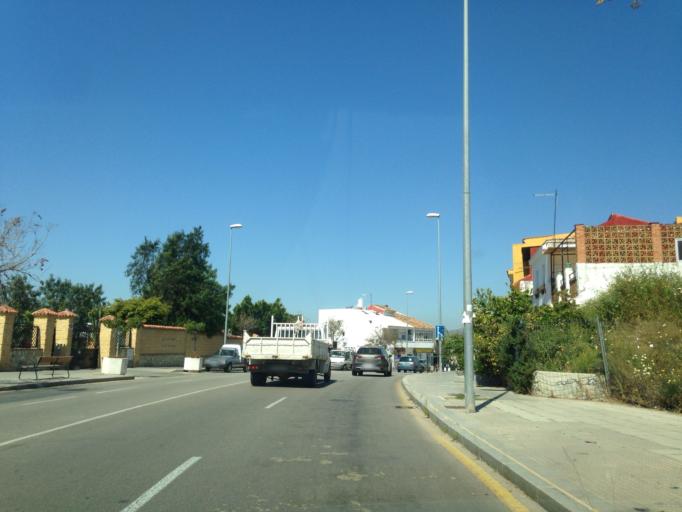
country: ES
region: Andalusia
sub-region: Provincia de Malaga
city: Malaga
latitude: 36.7333
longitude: -4.4769
